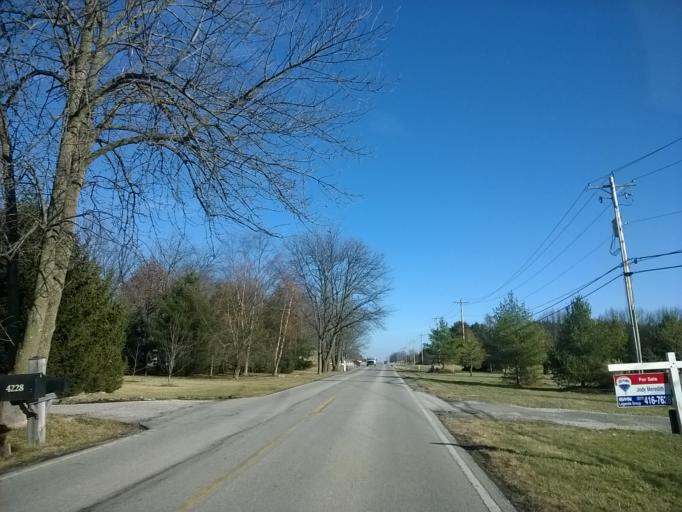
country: US
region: Indiana
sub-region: Boone County
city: Zionsville
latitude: 39.9771
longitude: -86.2342
